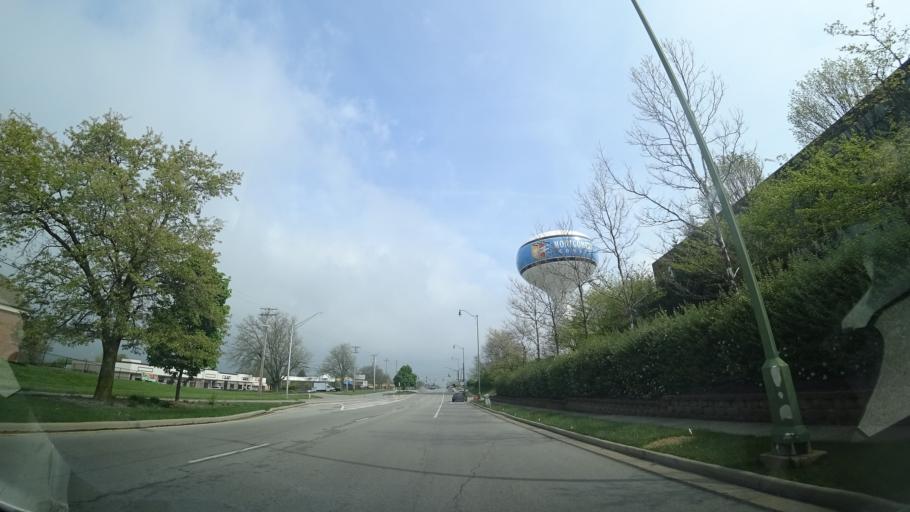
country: US
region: Ohio
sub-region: Greene County
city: Beavercreek
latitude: 39.6954
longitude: -84.1060
